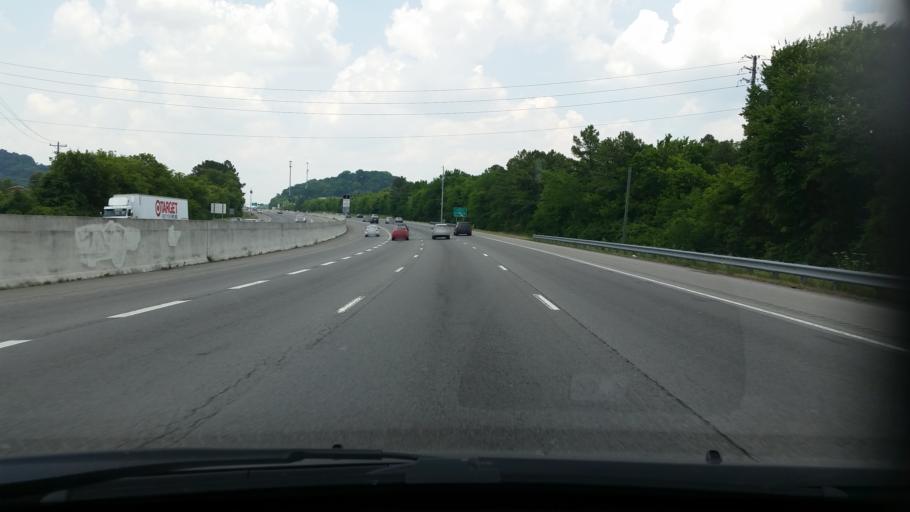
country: US
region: Tennessee
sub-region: Williamson County
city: Brentwood Estates
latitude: 36.0262
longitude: -86.7847
